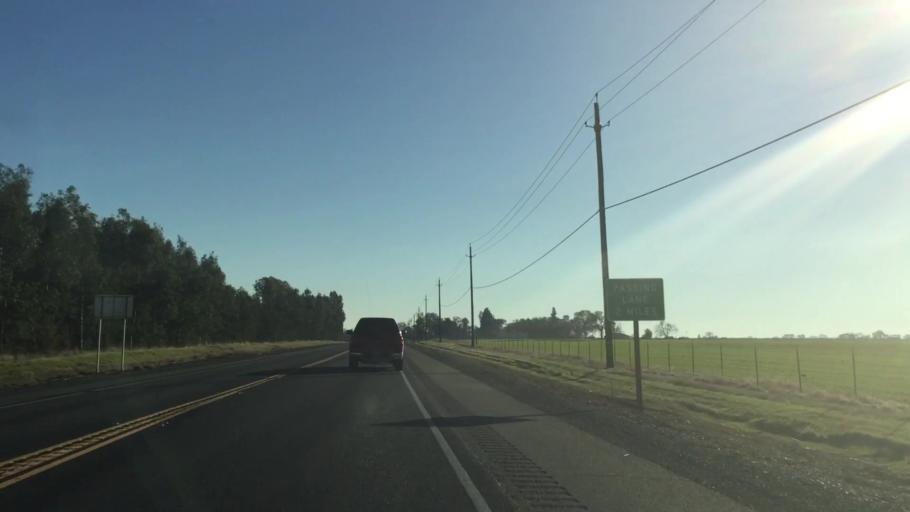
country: US
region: California
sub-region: Butte County
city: Palermo
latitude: 39.4142
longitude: -121.6050
